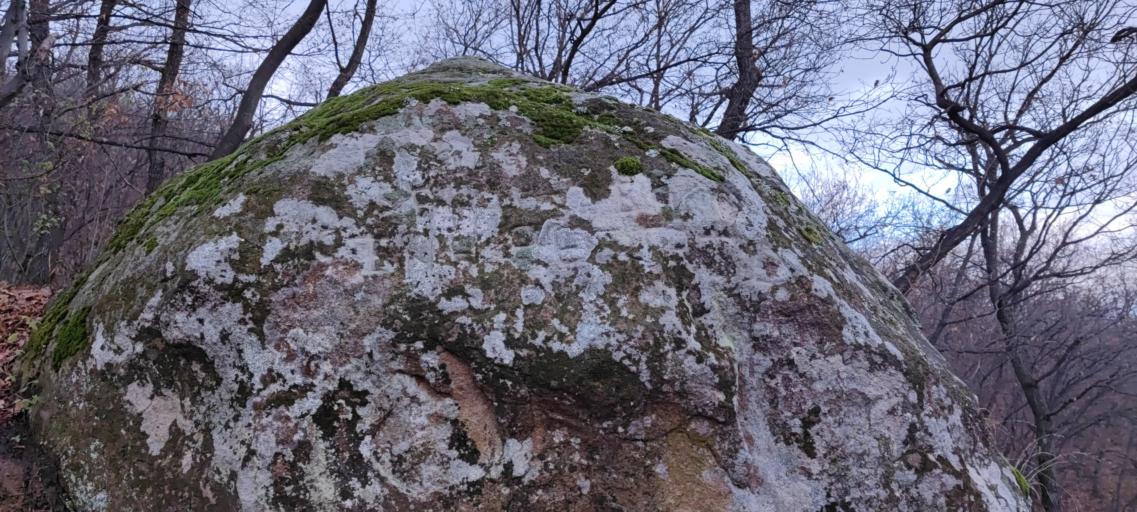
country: BG
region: Plovdiv
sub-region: Obshtina Krichim
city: Krichim
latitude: 42.0357
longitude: 24.4630
